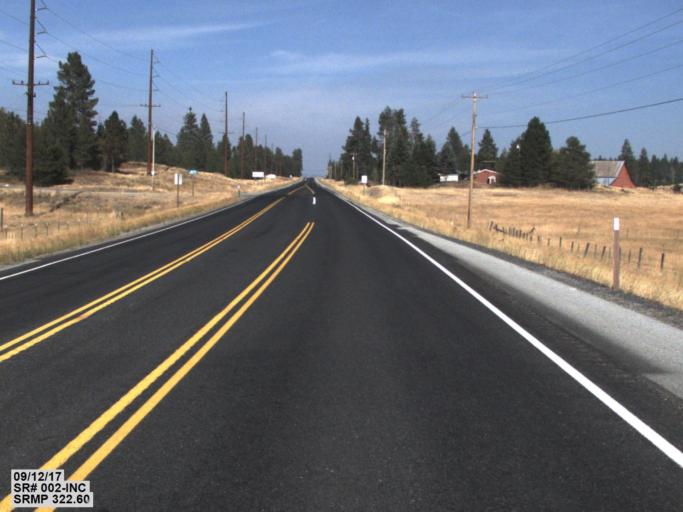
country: US
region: Washington
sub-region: Pend Oreille County
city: Newport
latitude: 48.0989
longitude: -117.2529
